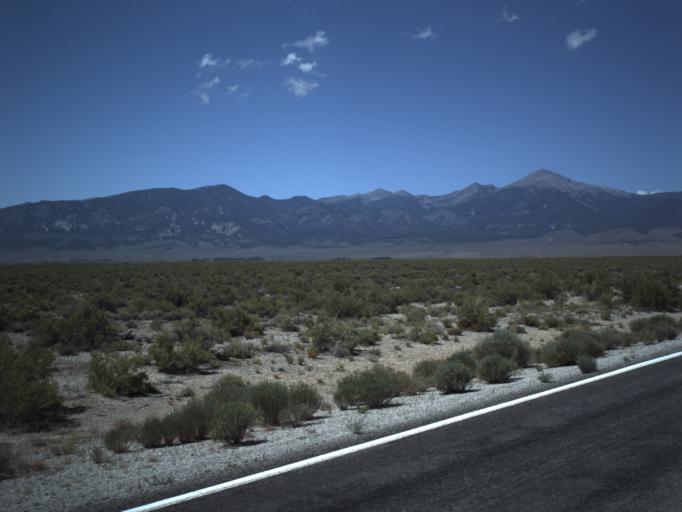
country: US
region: Nevada
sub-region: White Pine County
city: McGill
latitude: 39.0573
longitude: -114.0511
